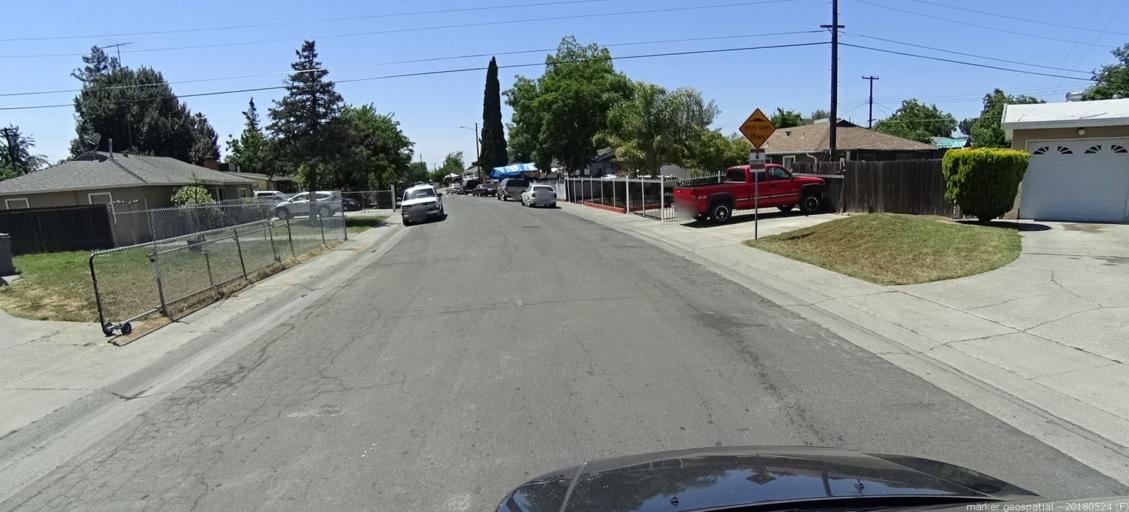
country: US
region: California
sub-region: Sacramento County
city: Sacramento
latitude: 38.6195
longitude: -121.4484
